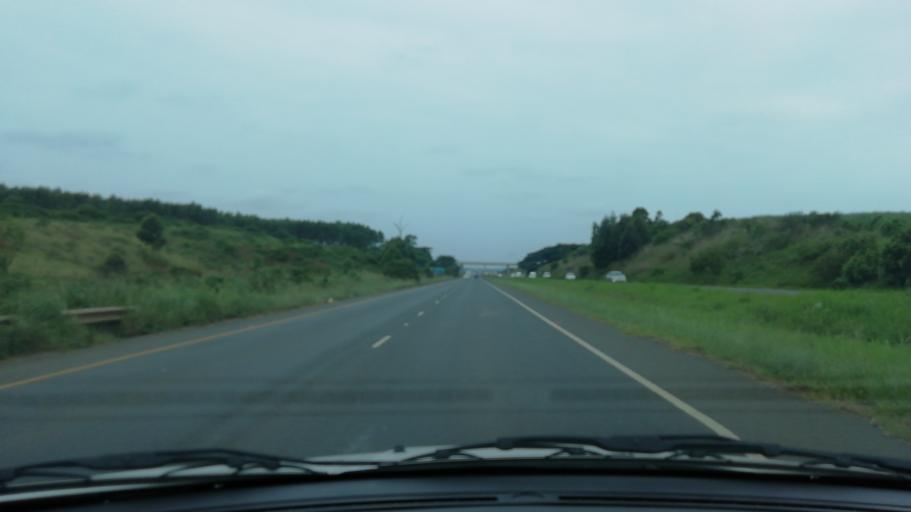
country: ZA
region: KwaZulu-Natal
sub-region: uThungulu District Municipality
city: Empangeni
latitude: -28.7676
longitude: 31.9253
